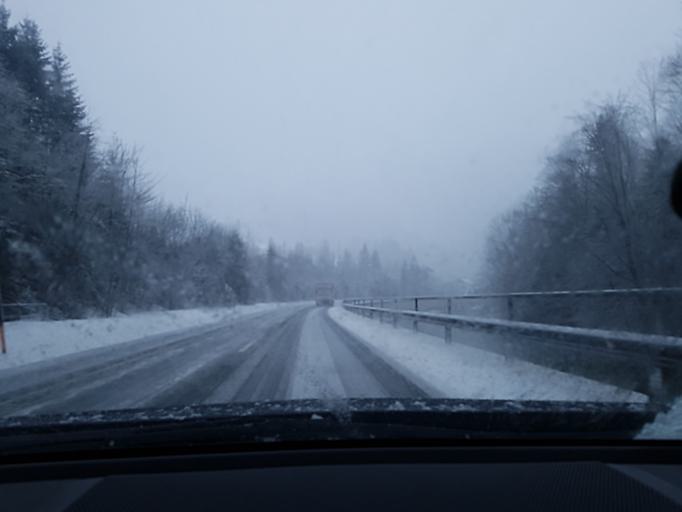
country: AT
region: Salzburg
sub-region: Politischer Bezirk Hallein
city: Abtenau
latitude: 47.5918
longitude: 13.2915
